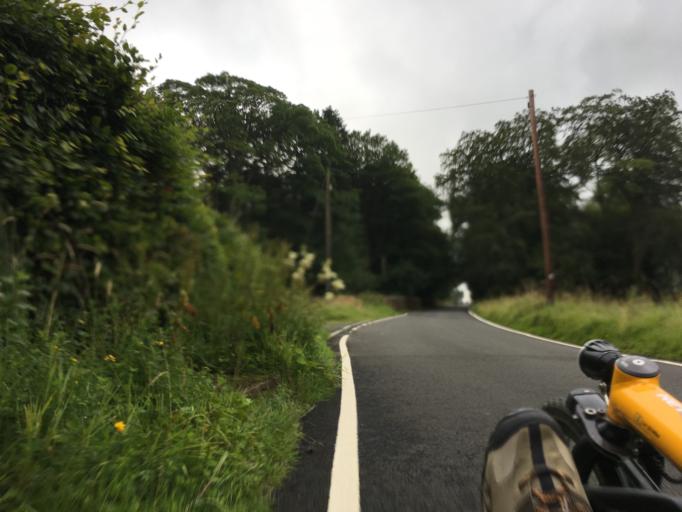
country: GB
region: Scotland
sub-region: West Lothian
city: West Calder
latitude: 55.8394
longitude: -3.5292
